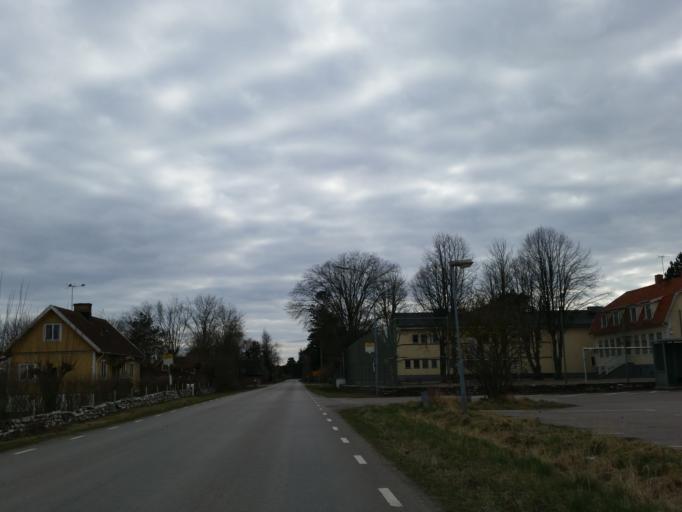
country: SE
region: Kalmar
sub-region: Morbylanga Kommun
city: Sodra Sandby
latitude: 56.5950
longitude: 16.6352
